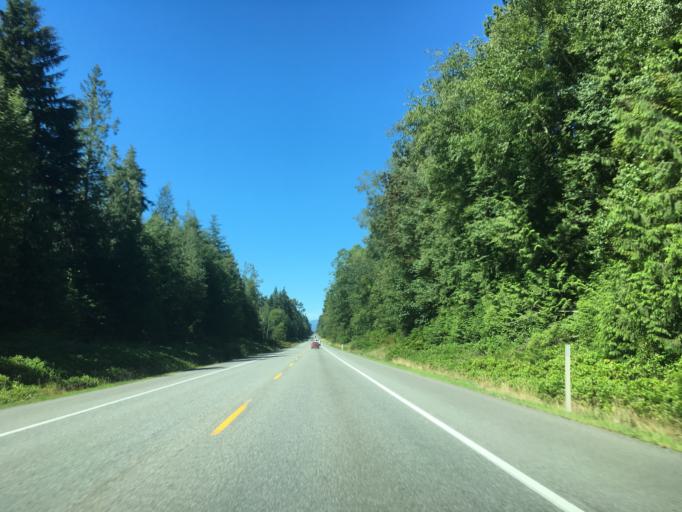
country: US
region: Washington
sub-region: Snohomish County
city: Sisco Heights
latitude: 48.0999
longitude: -122.1120
